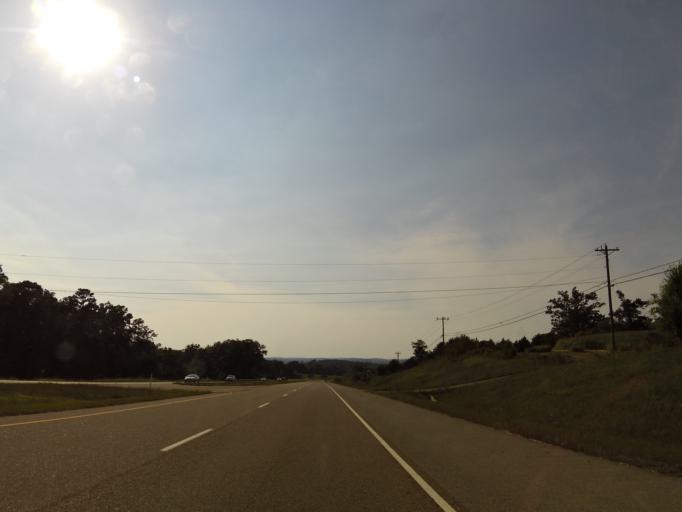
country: US
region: Tennessee
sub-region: Loudon County
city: Lenoir City
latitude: 35.7577
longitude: -84.2202
